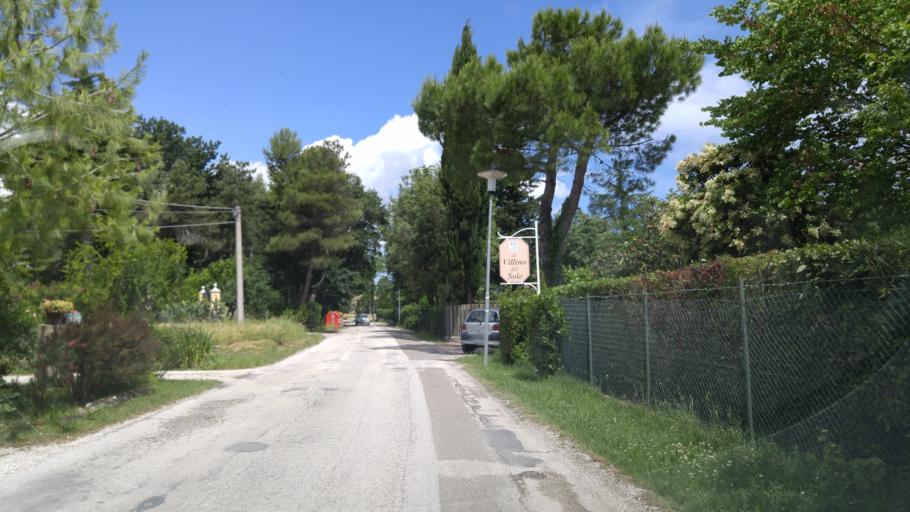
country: IT
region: The Marches
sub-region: Provincia di Pesaro e Urbino
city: Bellocchi
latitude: 43.8027
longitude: 13.0076
